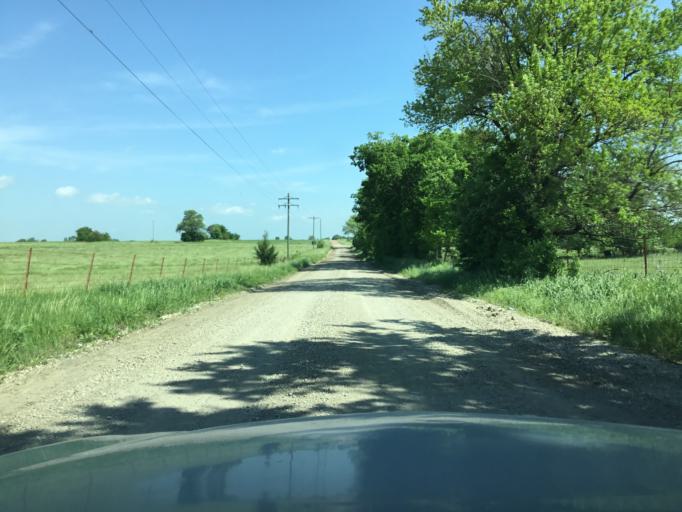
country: US
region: Kansas
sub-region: Labette County
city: Oswego
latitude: 37.1766
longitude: -95.1399
